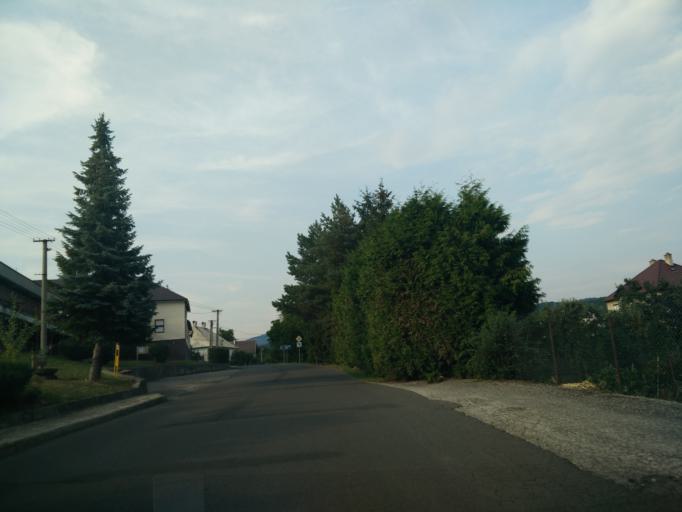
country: SK
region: Banskobystricky
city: Ziar nad Hronom
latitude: 48.6563
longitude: 18.8349
